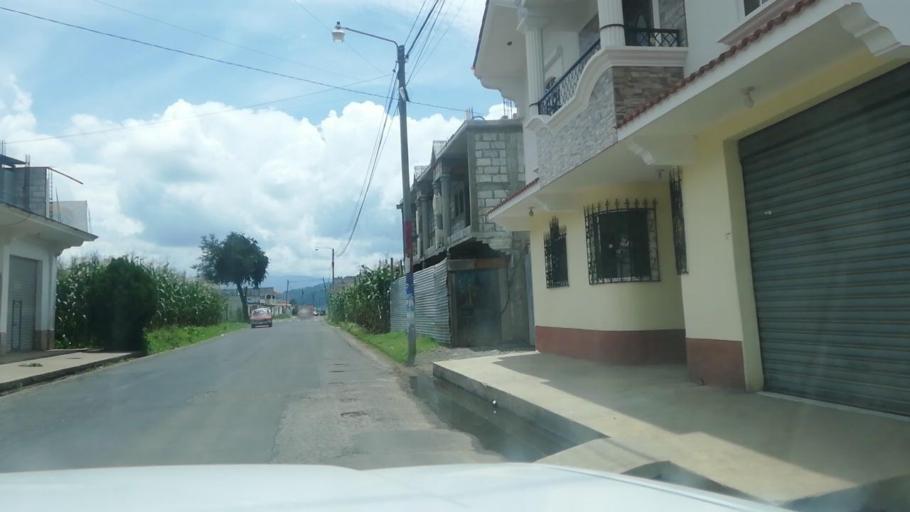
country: GT
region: Totonicapan
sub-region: Municipio de San Andres Xecul
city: San Andres Xecul
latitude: 14.9052
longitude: -91.4688
